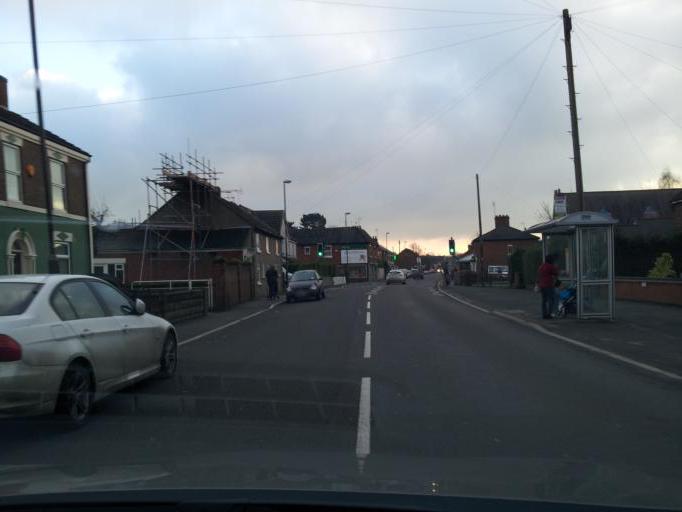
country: GB
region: England
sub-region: Staffordshire
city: Burton upon Trent
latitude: 52.8679
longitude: -1.6803
